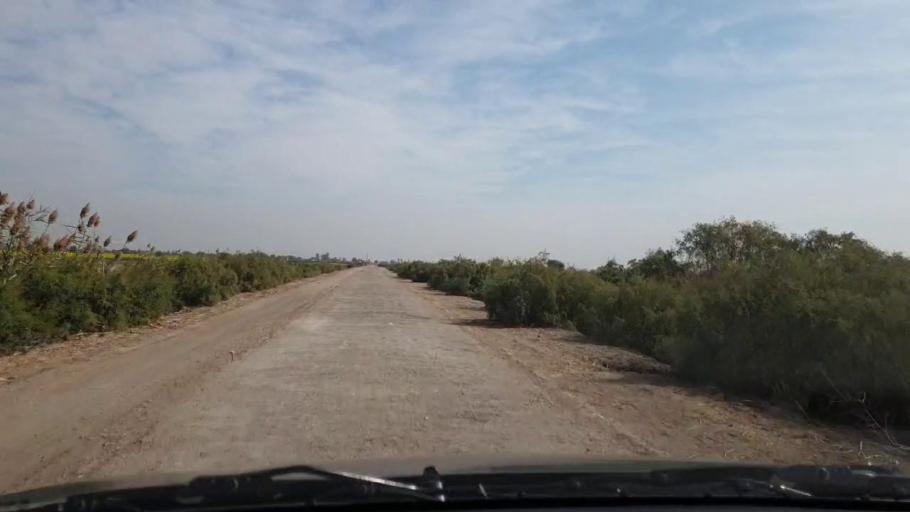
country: PK
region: Sindh
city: Jam Sahib
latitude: 26.2690
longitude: 68.7009
